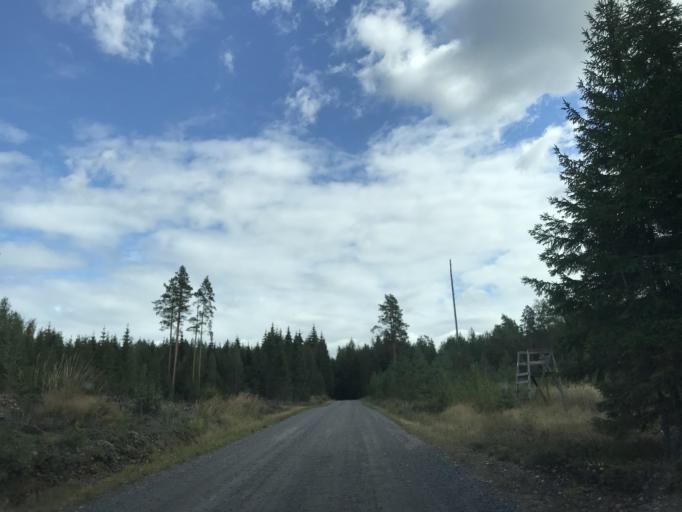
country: FI
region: Uusimaa
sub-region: Helsinki
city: Kaerkoelae
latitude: 60.6349
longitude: 23.7934
